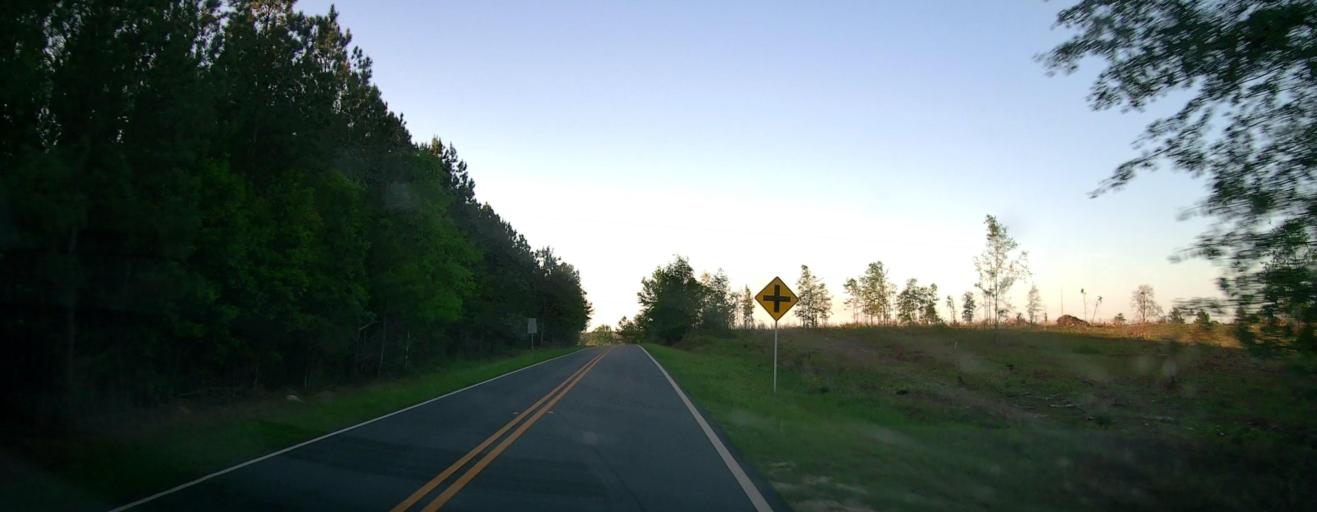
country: US
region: Georgia
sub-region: Marion County
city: Buena Vista
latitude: 32.4334
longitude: -84.4279
